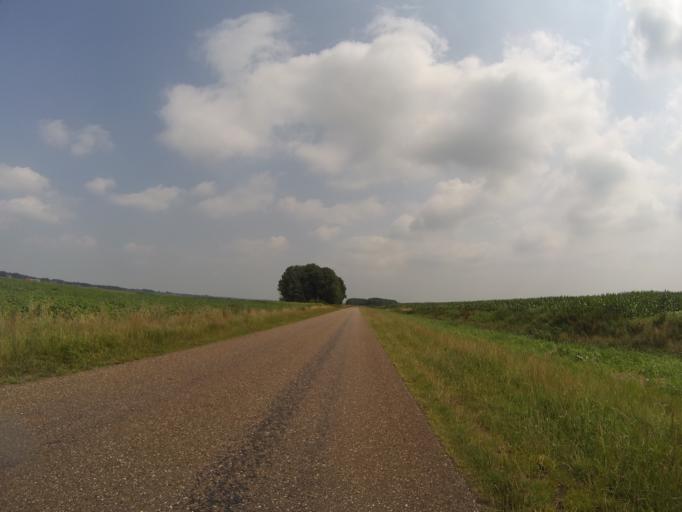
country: NL
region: Drenthe
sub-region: Gemeente Emmen
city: Emmer-Compascuum
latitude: 52.8725
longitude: 6.9753
